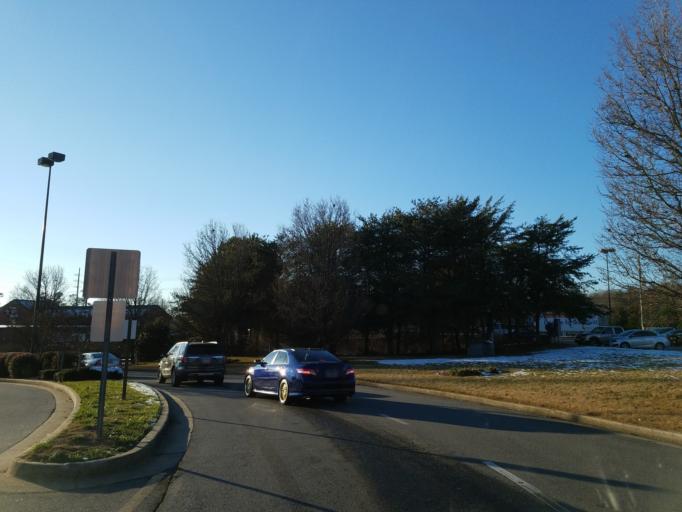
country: US
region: Georgia
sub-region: Dawson County
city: Dawsonville
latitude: 34.3549
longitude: -84.0497
